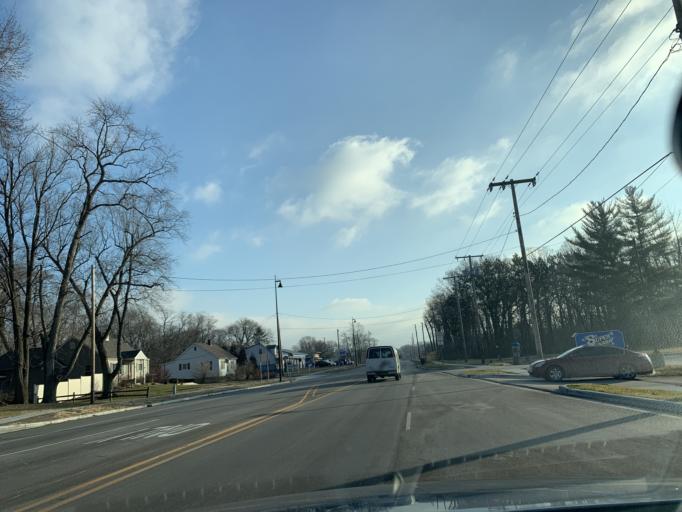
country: US
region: Indiana
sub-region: Porter County
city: Portage
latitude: 41.5759
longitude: -87.1683
